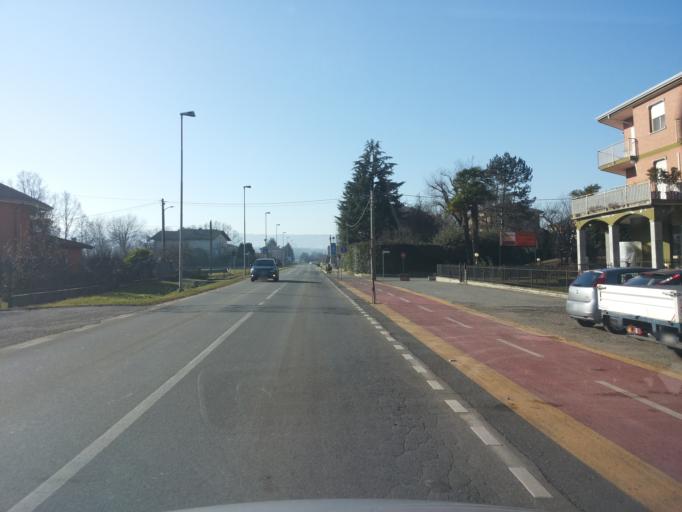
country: IT
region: Piedmont
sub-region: Provincia di Biella
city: Vergnasco
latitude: 45.4871
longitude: 8.0855
